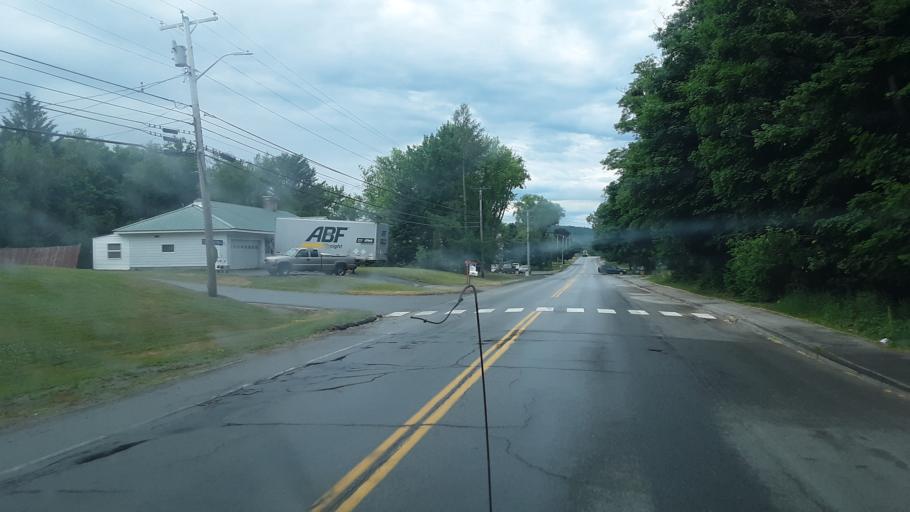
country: US
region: Maine
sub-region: Penobscot County
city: Lincoln
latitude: 45.3744
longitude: -68.5016
